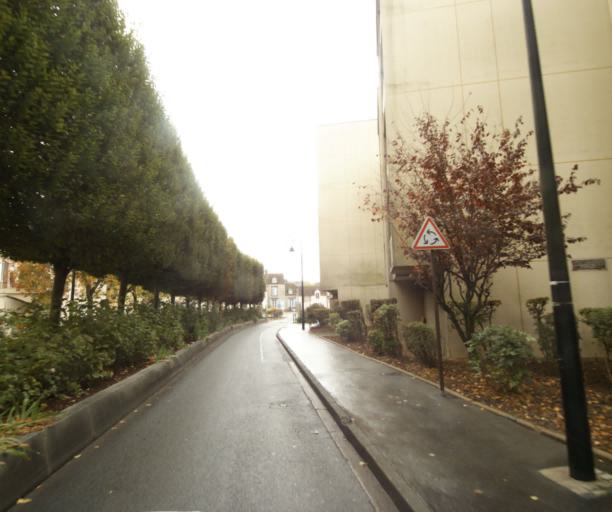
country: FR
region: Centre
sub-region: Departement d'Eure-et-Loir
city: Dreux
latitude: 48.7339
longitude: 1.3641
